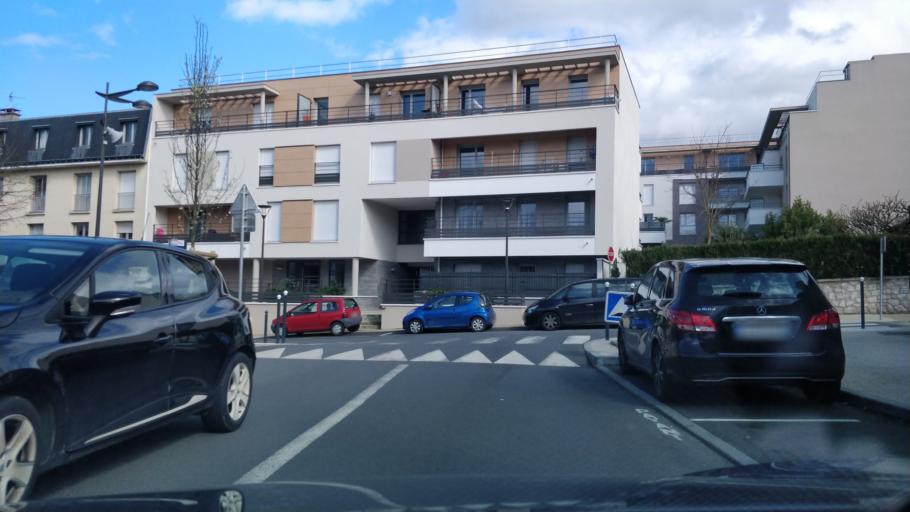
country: FR
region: Ile-de-France
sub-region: Departement de l'Essonne
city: Bures-sur-Yvette
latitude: 48.6960
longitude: 2.1624
